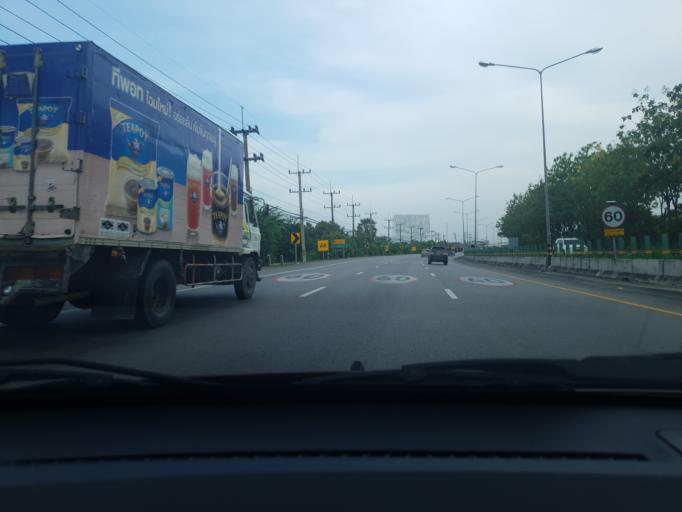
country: TH
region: Phetchaburi
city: Phetchaburi
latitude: 13.1283
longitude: 99.8718
